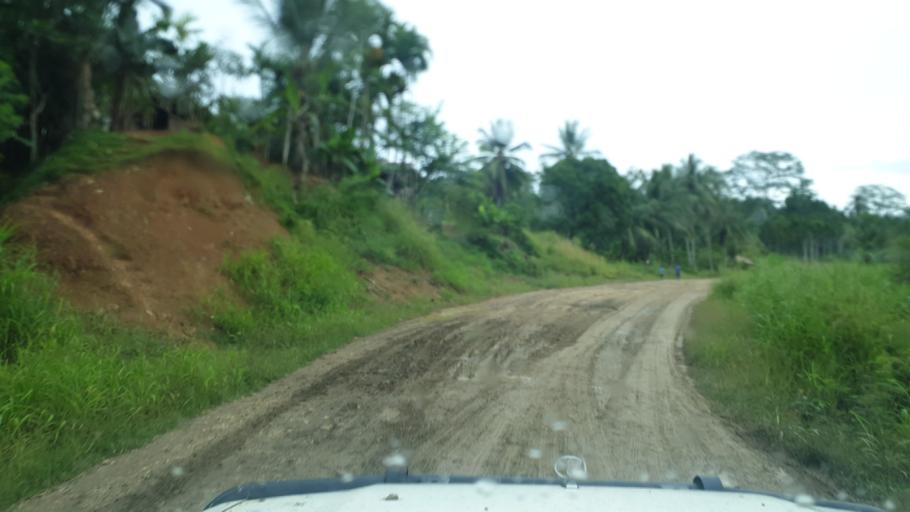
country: PG
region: Gulf
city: Kerema
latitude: -7.9803
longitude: 145.7969
